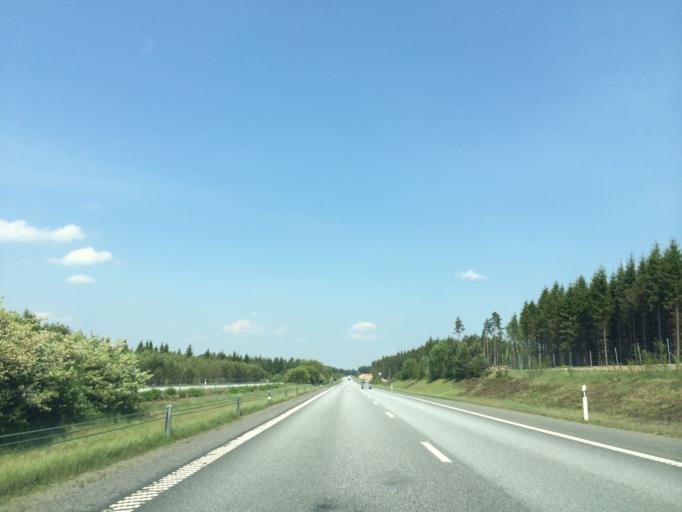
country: SE
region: Joenkoeping
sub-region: Varnamo Kommun
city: Varnamo
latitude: 57.2180
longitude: 14.0834
